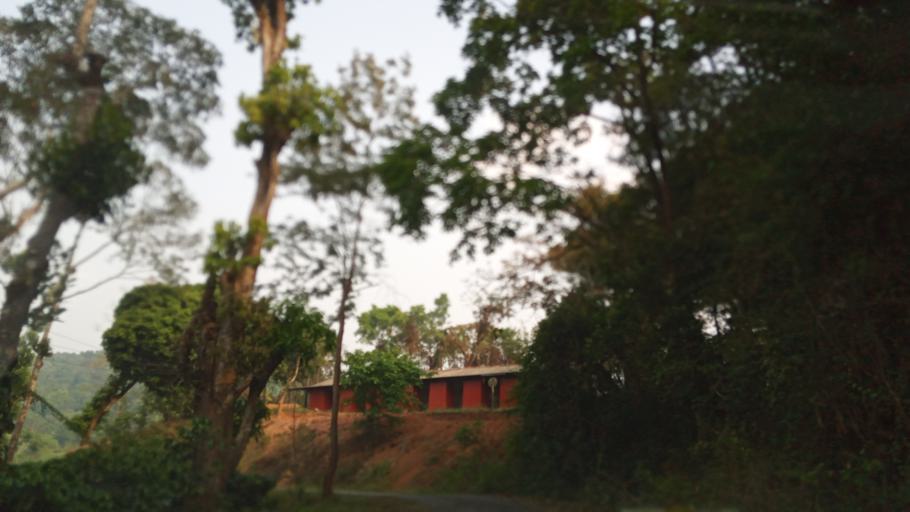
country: IN
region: Karnataka
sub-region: Chikmagalur
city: Mudigere
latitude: 13.0147
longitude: 75.6277
